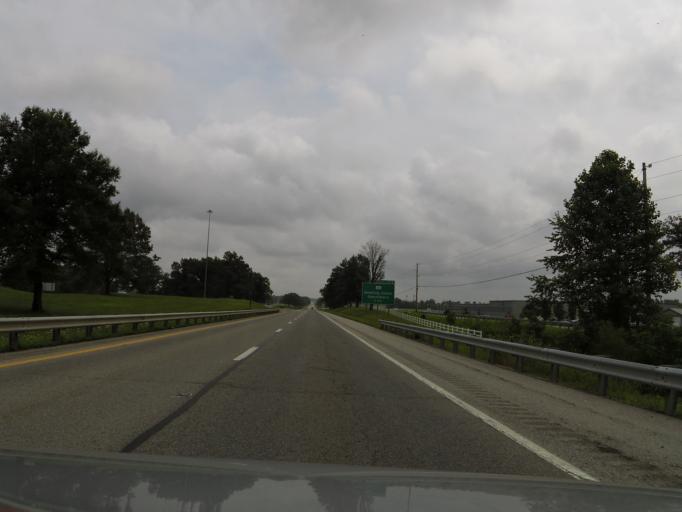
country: US
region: Kentucky
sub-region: Ohio County
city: Beaver Dam
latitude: 37.3721
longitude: -86.8335
